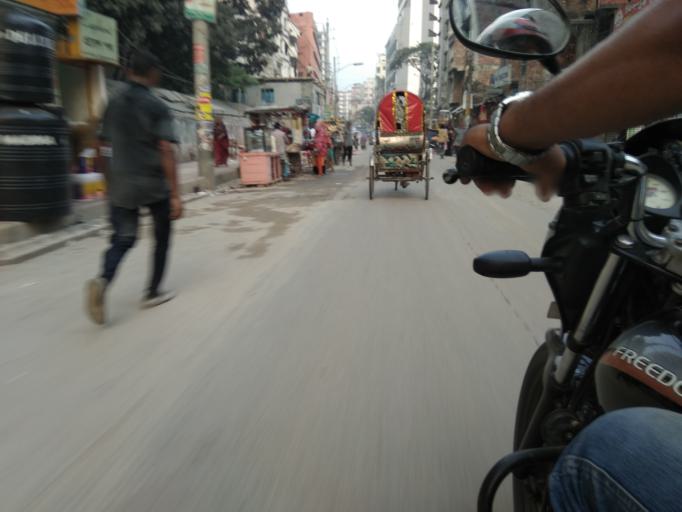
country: BD
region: Dhaka
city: Tungi
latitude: 23.8185
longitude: 90.3630
